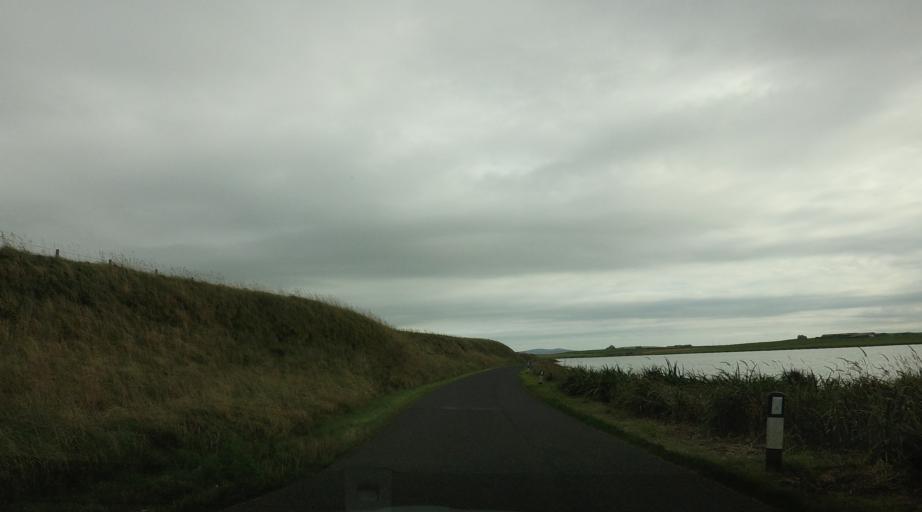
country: GB
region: Scotland
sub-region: Orkney Islands
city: Stromness
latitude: 59.0465
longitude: -3.3214
